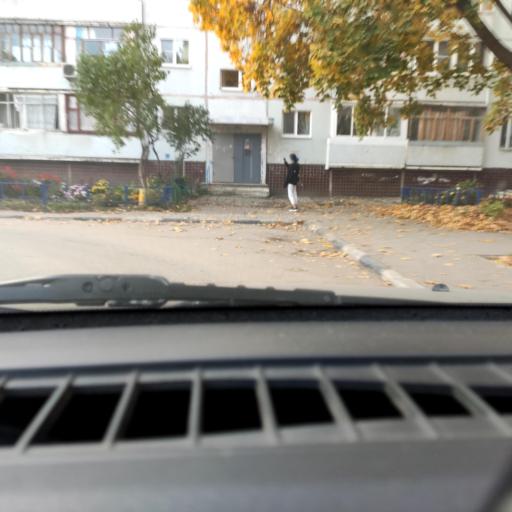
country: RU
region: Samara
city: Tol'yatti
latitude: 53.5289
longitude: 49.2928
